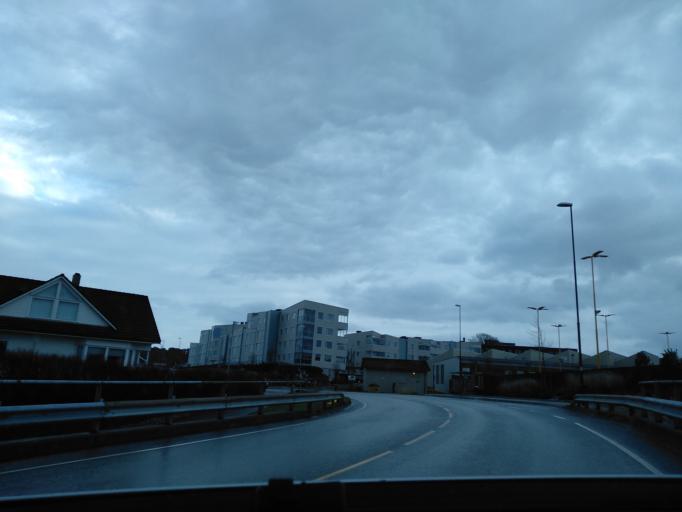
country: NO
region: Rogaland
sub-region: Stavanger
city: Stavanger
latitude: 58.9900
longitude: 5.6893
